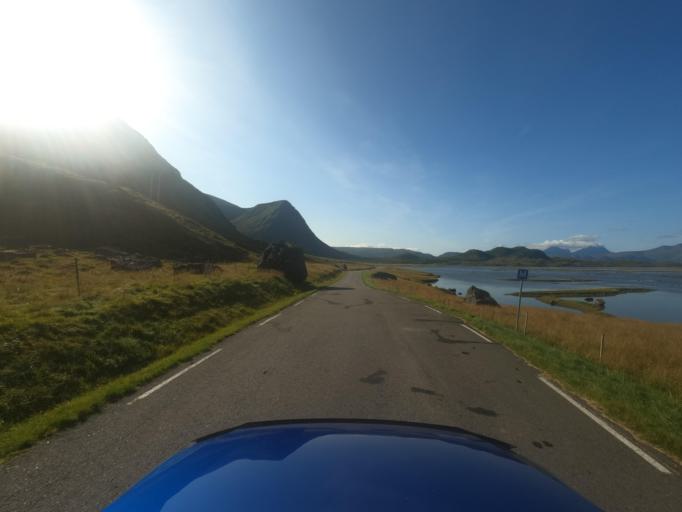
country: NO
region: Nordland
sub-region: Vestvagoy
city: Evjen
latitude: 68.3344
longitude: 13.9206
